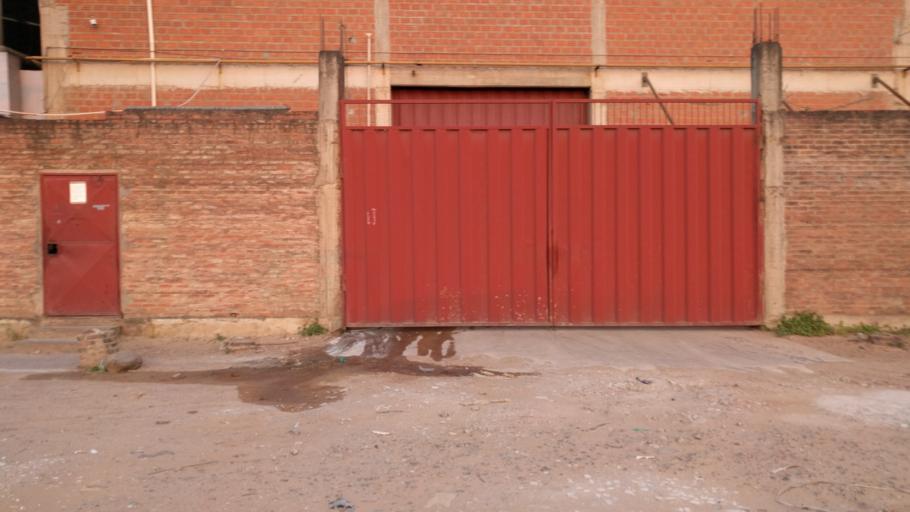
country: BO
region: Santa Cruz
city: Santa Cruz de la Sierra
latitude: -17.7574
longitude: -63.1473
